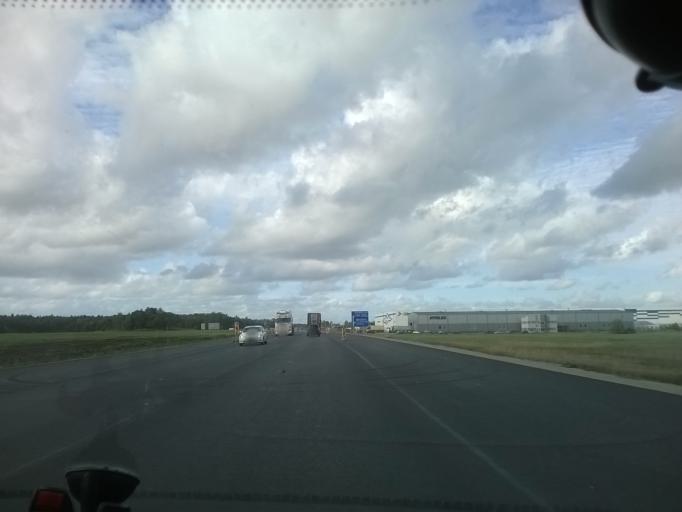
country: EE
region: Harju
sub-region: Rae vald
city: Jueri
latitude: 59.3909
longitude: 24.9196
